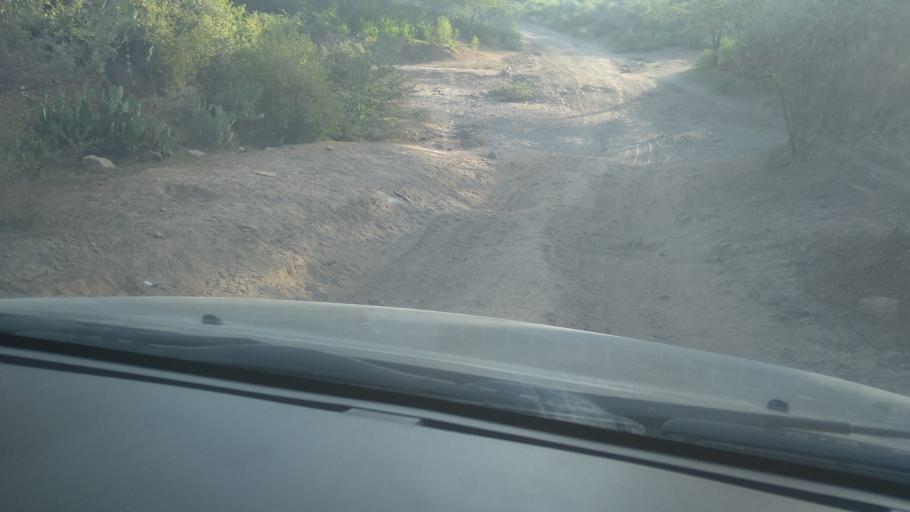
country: ET
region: Oromiya
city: Hirna
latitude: 9.3726
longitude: 40.9092
